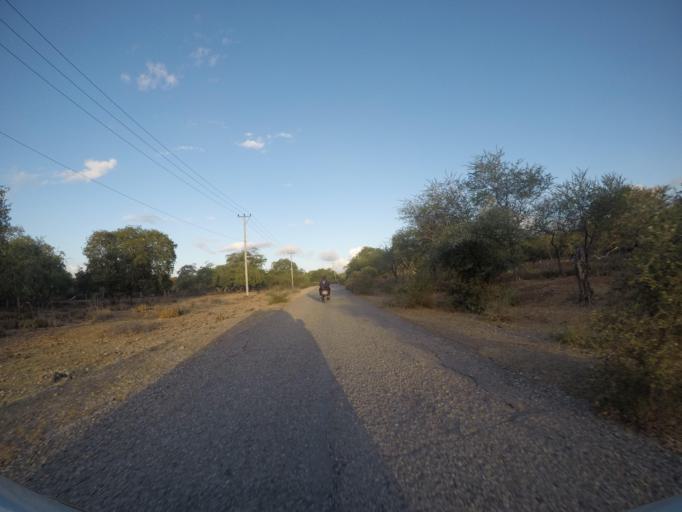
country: TL
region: Lautem
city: Lospalos
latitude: -8.3271
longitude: 126.9969
